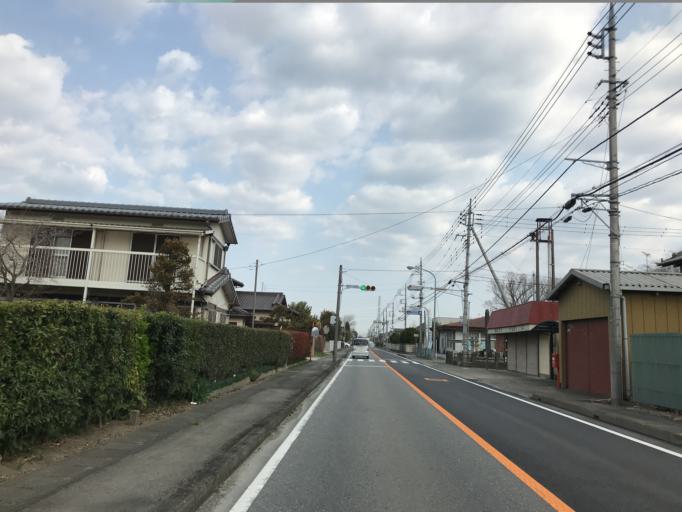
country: JP
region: Ibaraki
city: Mitsukaido
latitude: 36.0104
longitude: 140.0120
